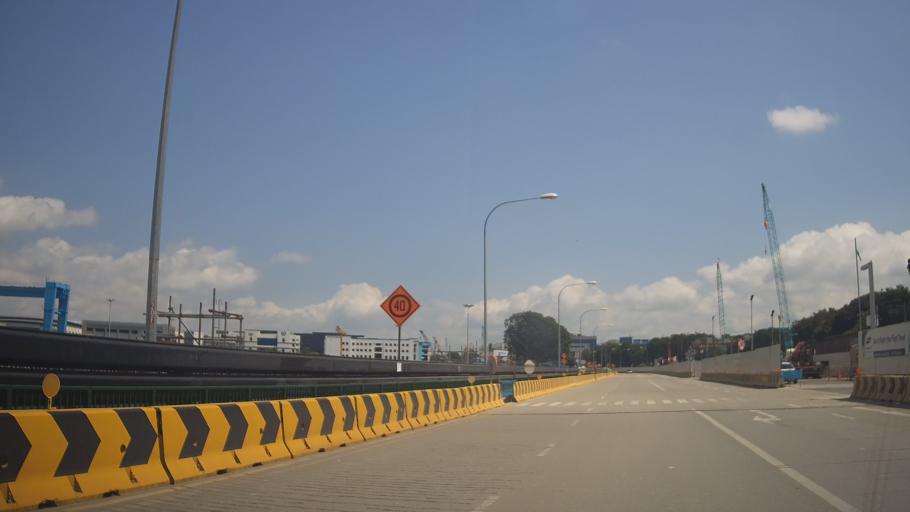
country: SG
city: Singapore
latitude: 1.3244
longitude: 103.9619
